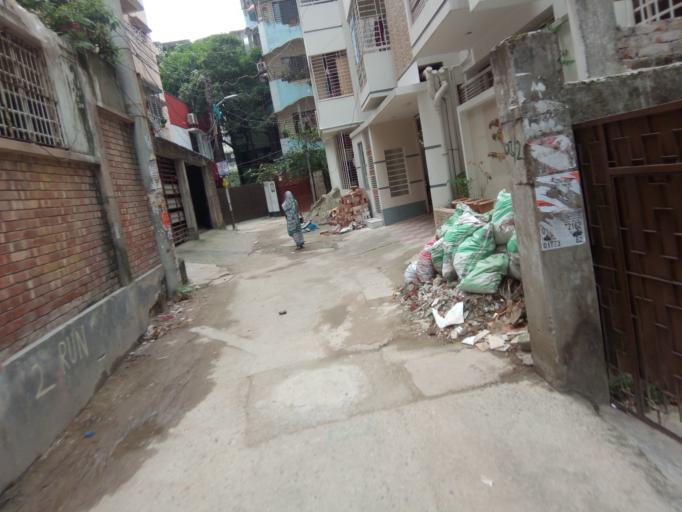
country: BD
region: Dhaka
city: Paltan
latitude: 23.7392
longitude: 90.4126
